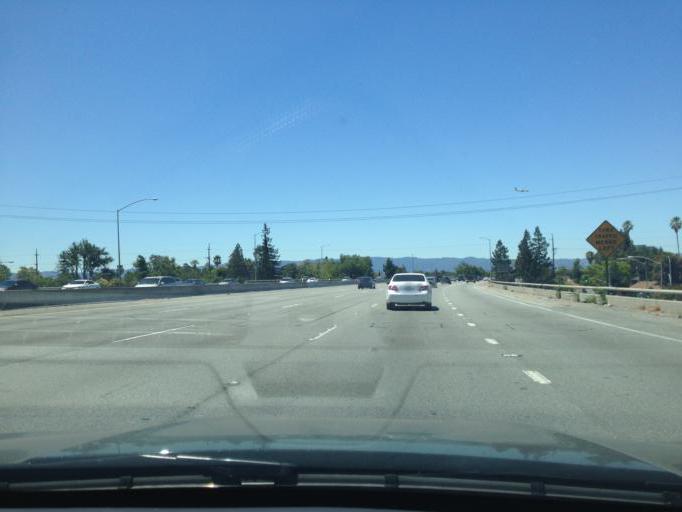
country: US
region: California
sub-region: Santa Clara County
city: San Jose
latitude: 37.3293
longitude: -121.8697
